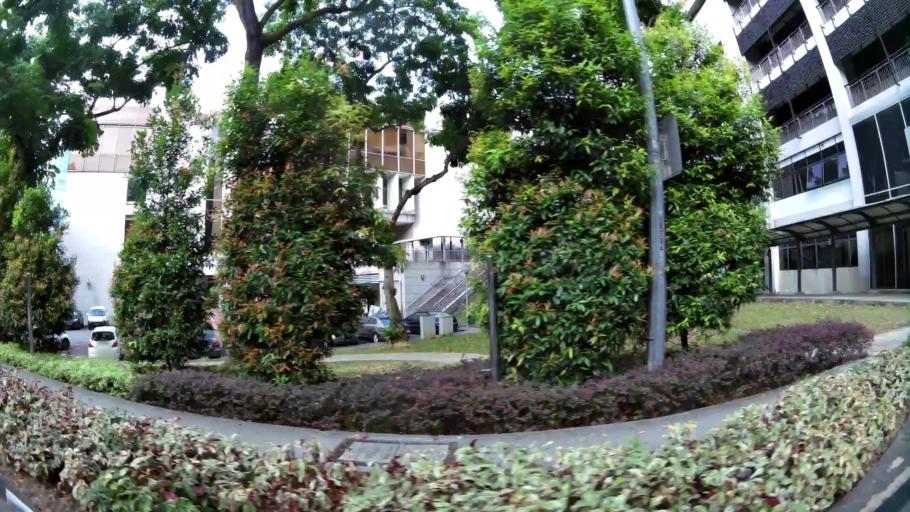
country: SG
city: Singapore
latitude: 1.2931
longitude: 103.7750
